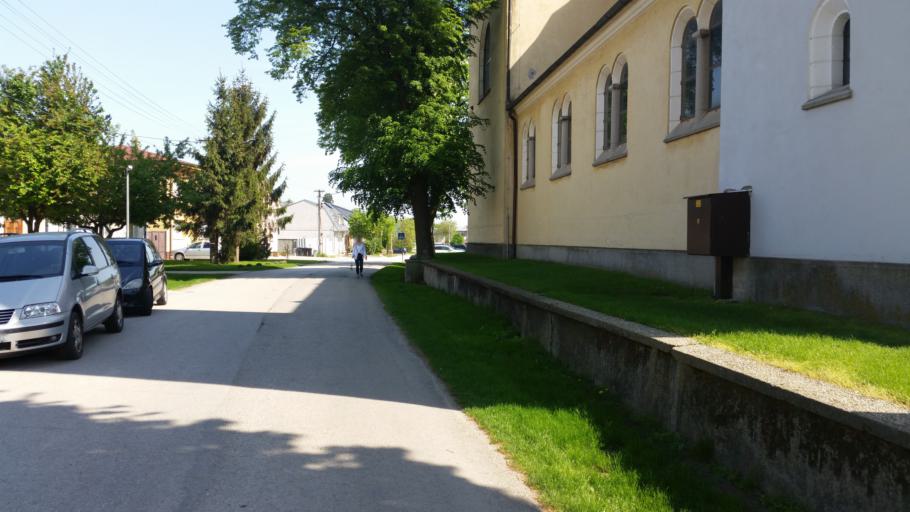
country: SK
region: Trnavsky
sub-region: Okres Trnava
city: Trnava
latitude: 48.3124
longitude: 17.4932
